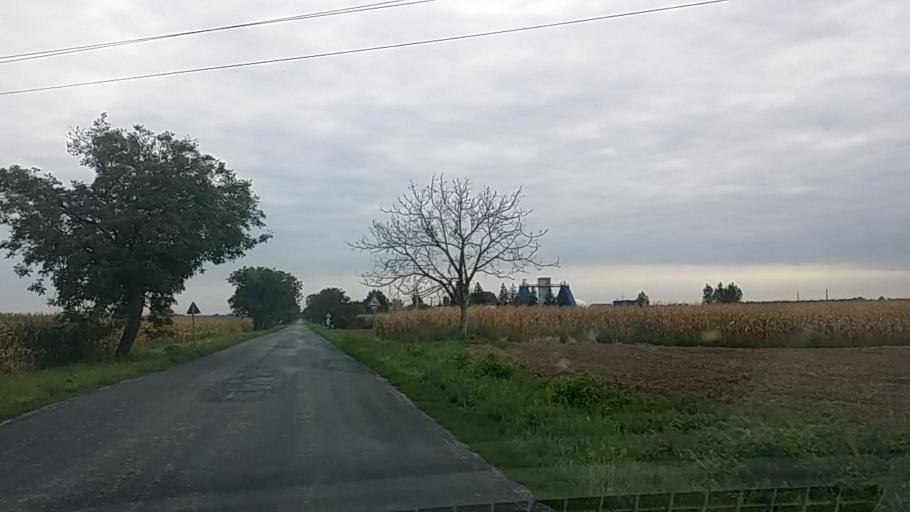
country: HU
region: Gyor-Moson-Sopron
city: Kapuvar
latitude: 47.6067
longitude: 17.0358
